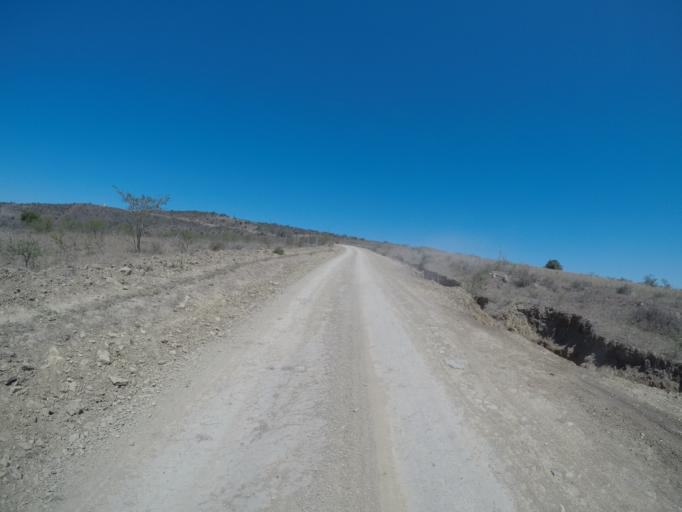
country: ZA
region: Eastern Cape
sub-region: OR Tambo District Municipality
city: Mthatha
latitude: -31.8744
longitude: 28.8725
